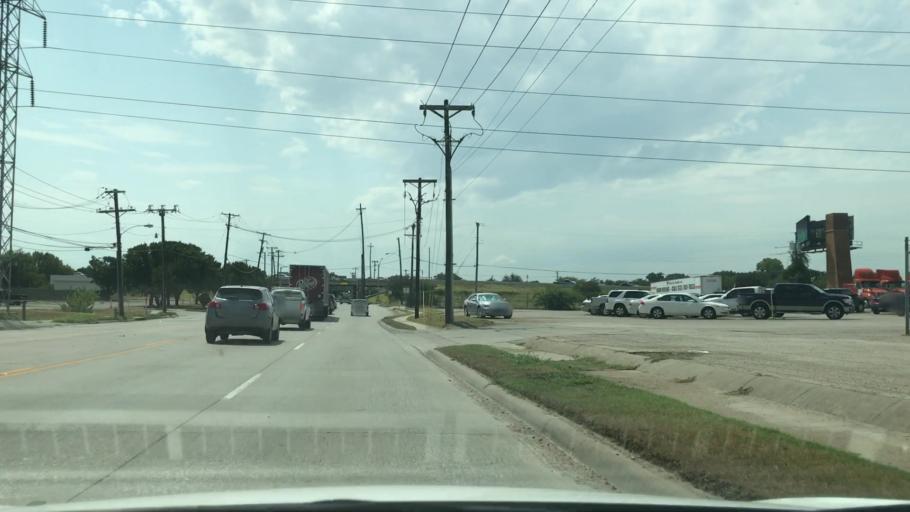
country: US
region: Texas
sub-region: Dallas County
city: Irving
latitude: 32.8308
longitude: -96.9142
